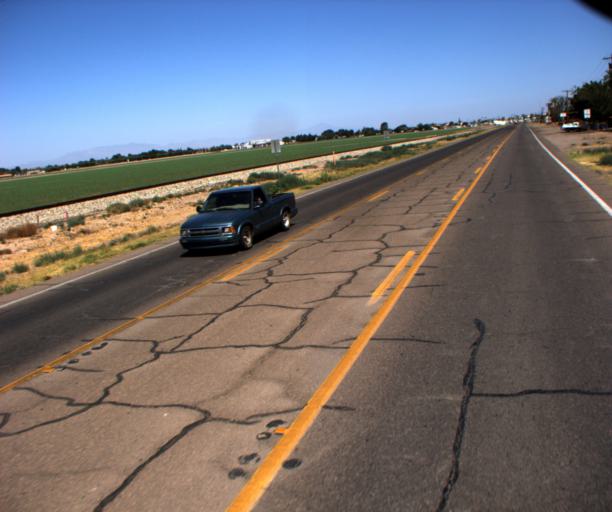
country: US
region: Arizona
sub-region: Graham County
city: Safford
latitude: 32.8258
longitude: -109.6920
